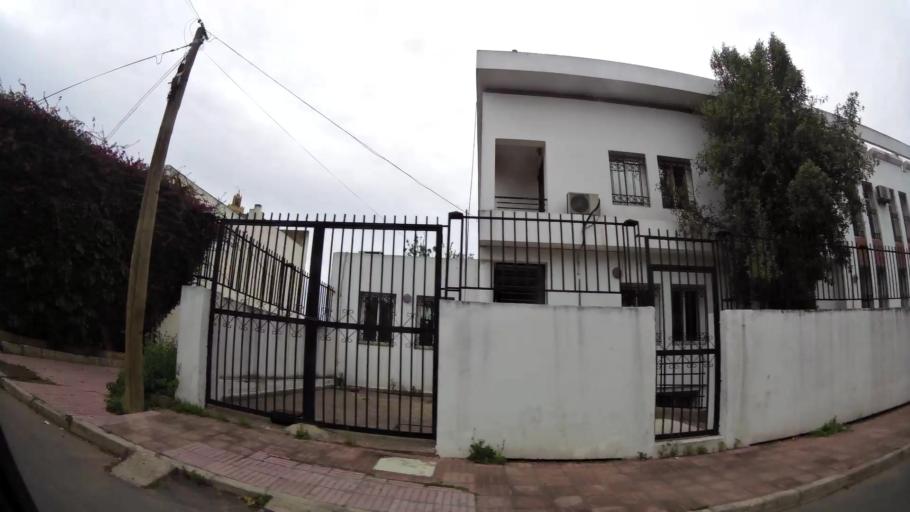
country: MA
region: Grand Casablanca
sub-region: Mediouna
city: Tit Mellil
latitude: 33.5640
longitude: -7.5337
